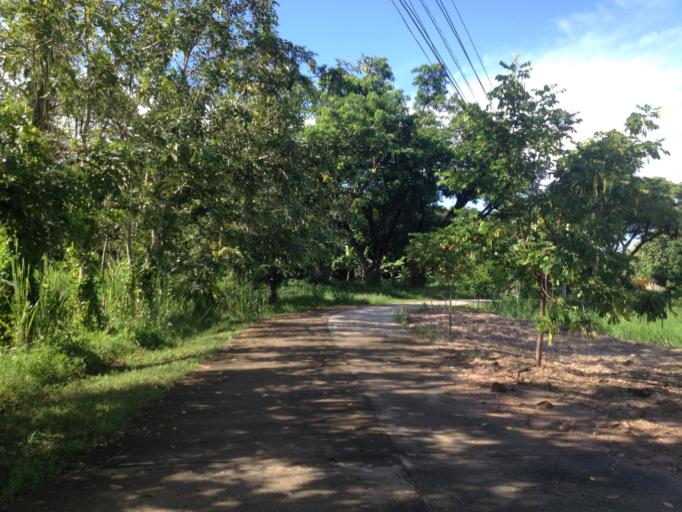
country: TH
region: Chiang Mai
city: Hang Dong
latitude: 18.6943
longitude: 98.9003
